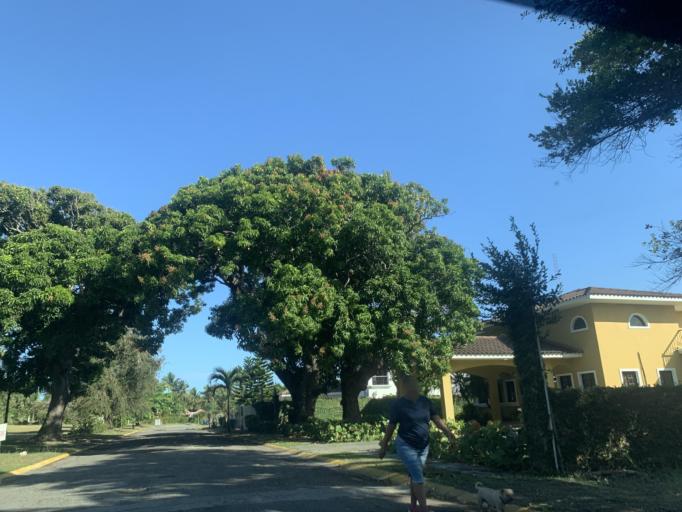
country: DO
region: Puerto Plata
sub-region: Puerto Plata
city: Puerto Plata
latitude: 19.8108
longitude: -70.7180
